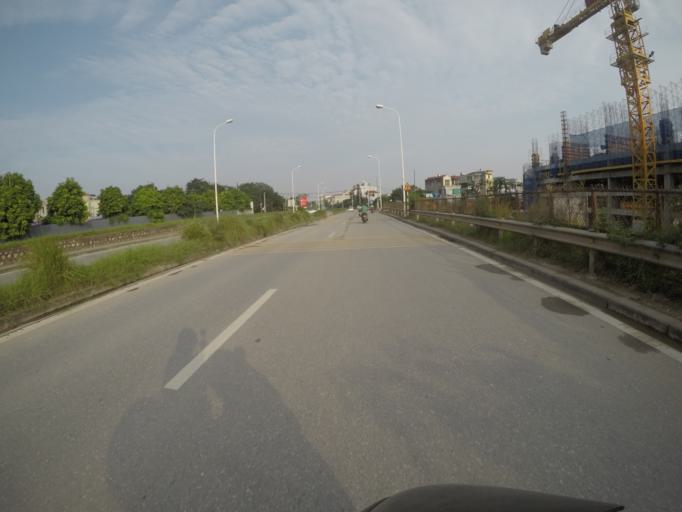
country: VN
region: Ha Noi
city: Tay Ho
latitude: 21.0898
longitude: 105.7947
